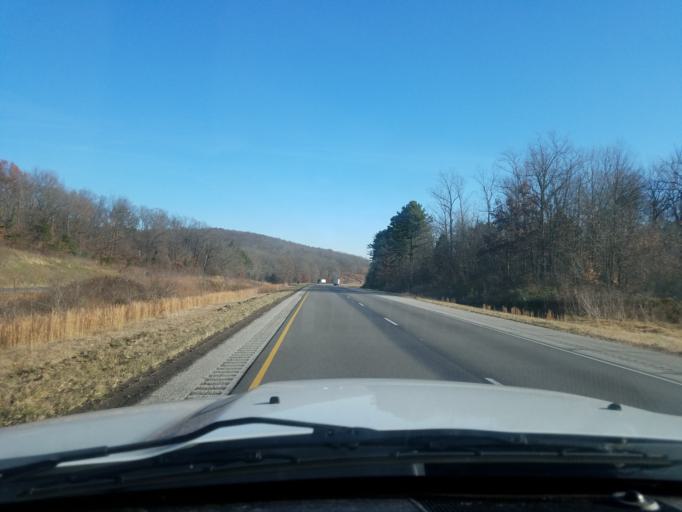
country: US
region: Indiana
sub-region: Crawford County
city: English
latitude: 38.2309
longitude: -86.5667
